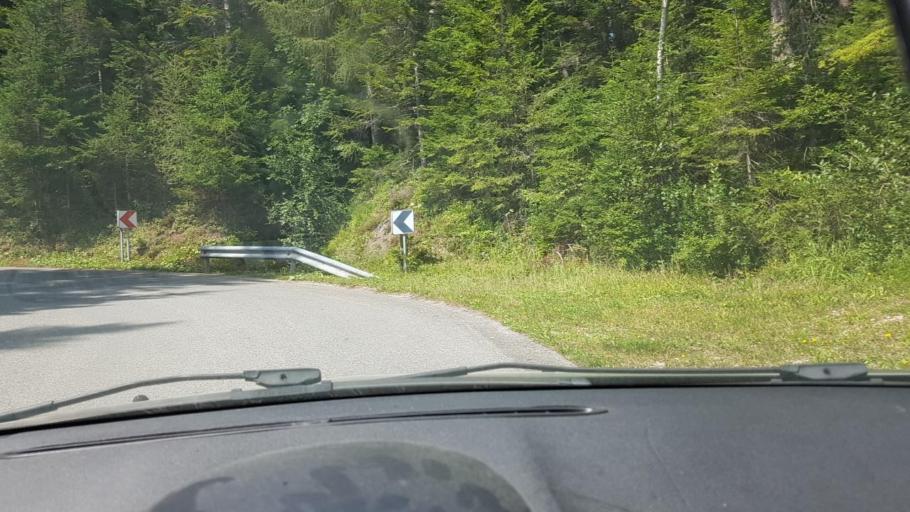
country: AT
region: Carinthia
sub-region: Politischer Bezirk Volkermarkt
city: Bad Eisenkappel
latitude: 46.4272
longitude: 14.5990
